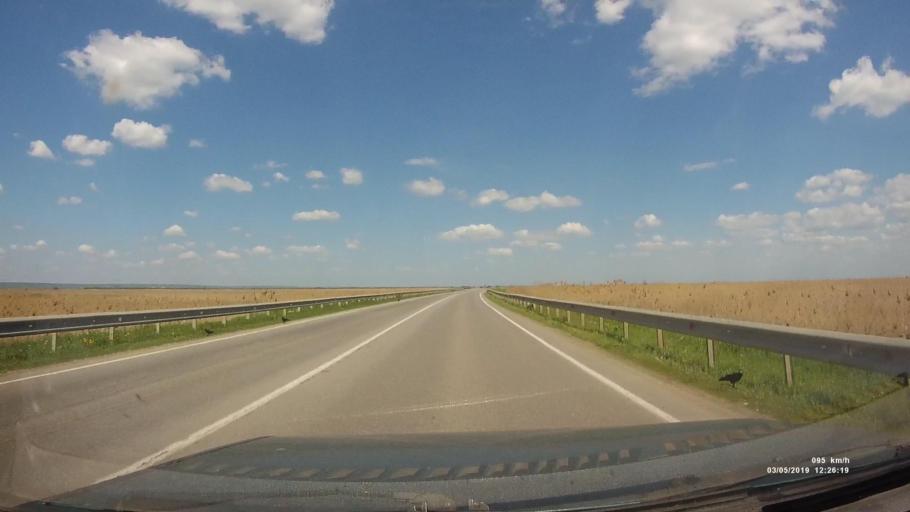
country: RU
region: Rostov
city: Semikarakorsk
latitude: 47.4435
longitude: 40.7129
